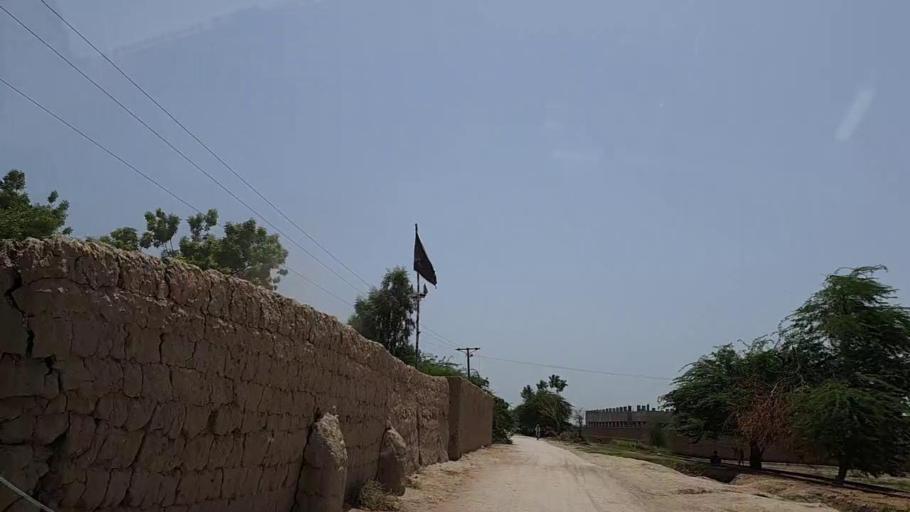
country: PK
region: Sindh
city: Tharu Shah
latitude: 26.9407
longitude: 68.1072
